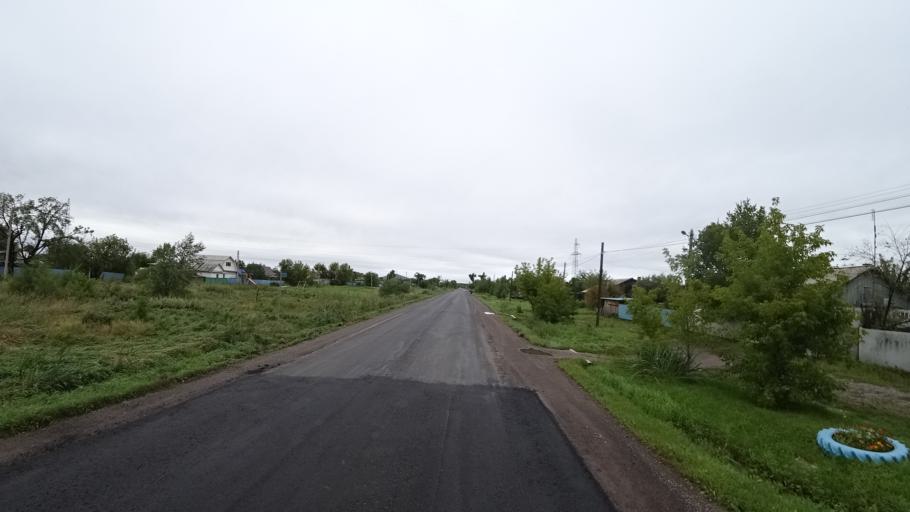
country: RU
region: Primorskiy
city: Monastyrishche
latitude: 44.1991
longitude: 132.4773
